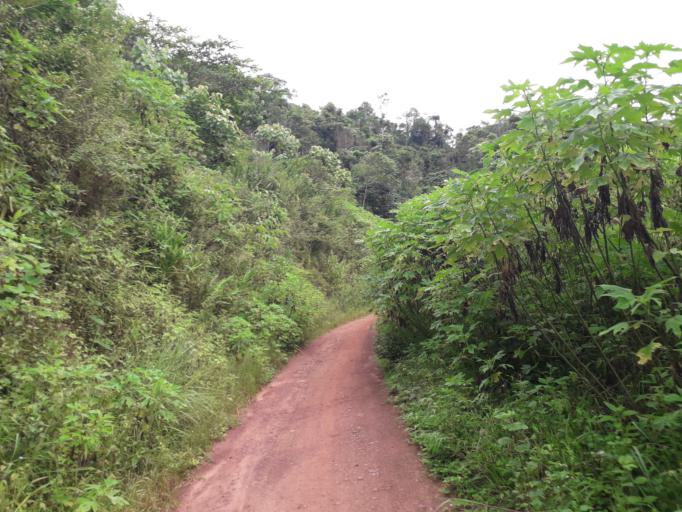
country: CN
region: Yunnan
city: Menglie
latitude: 22.2407
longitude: 101.6163
